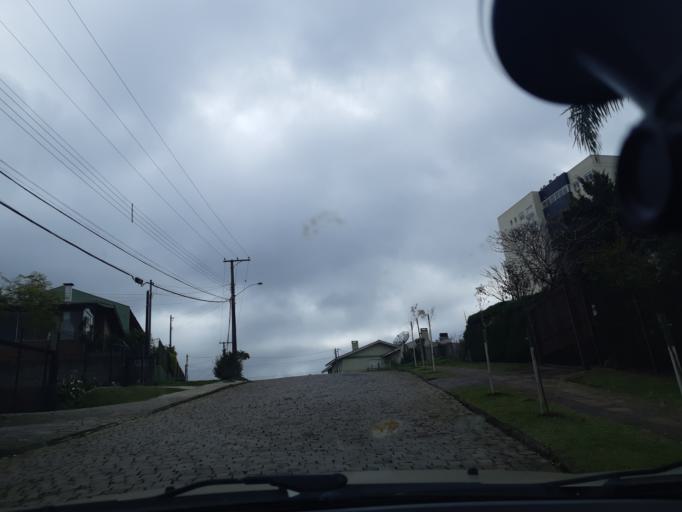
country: BR
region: Rio Grande do Sul
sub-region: Caxias Do Sul
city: Caxias do Sul
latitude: -29.1561
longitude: -51.2067
